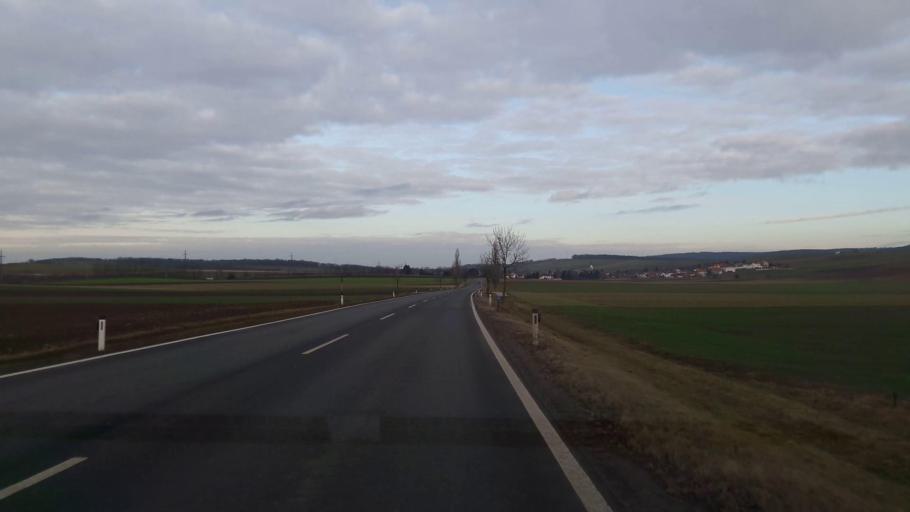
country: AT
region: Lower Austria
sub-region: Politischer Bezirk Mistelbach
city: Mistelbach
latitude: 48.5940
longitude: 16.5472
